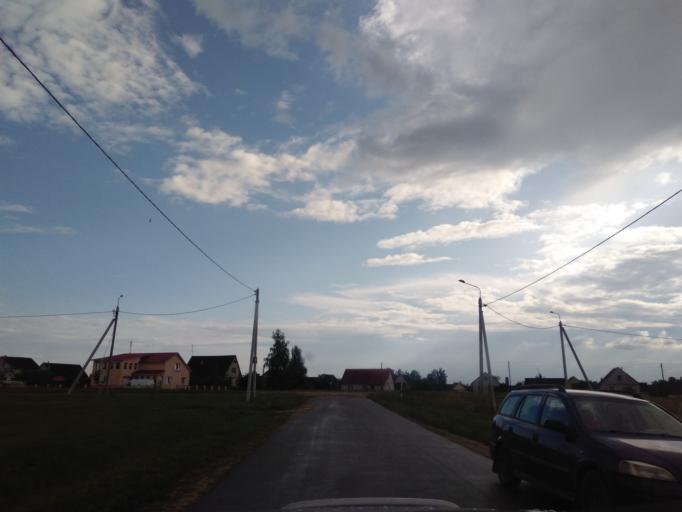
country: BY
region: Minsk
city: Kapyl'
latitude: 53.1616
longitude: 27.0756
